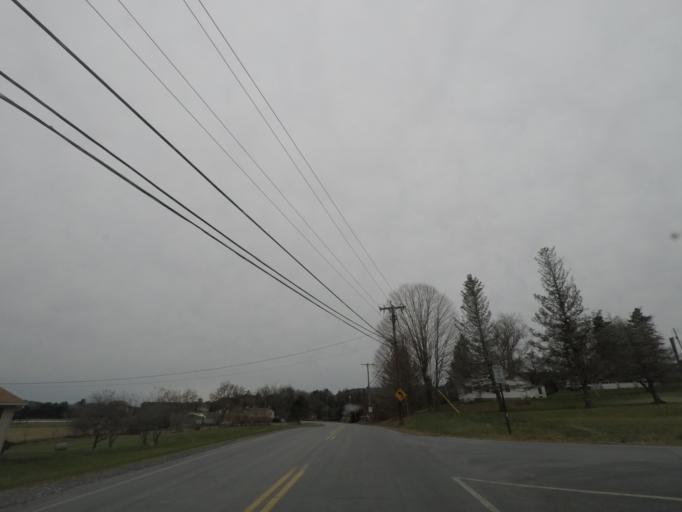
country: US
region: Massachusetts
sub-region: Berkshire County
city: Lanesborough
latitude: 42.5514
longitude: -73.3849
